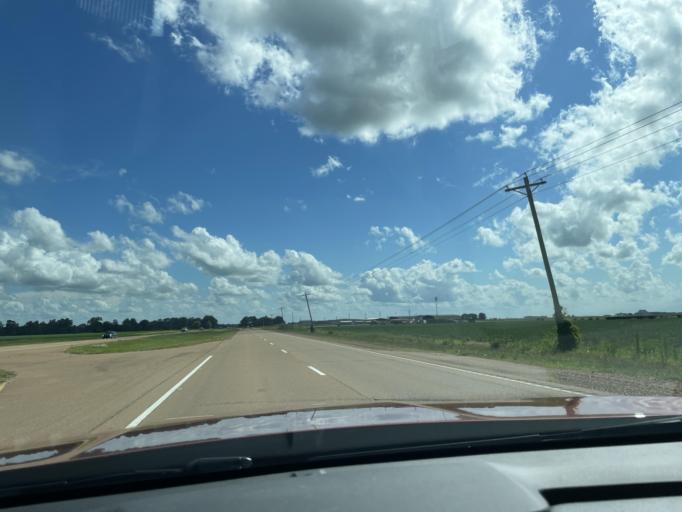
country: US
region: Mississippi
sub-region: Humphreys County
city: Belzoni
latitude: 33.1474
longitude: -90.5101
